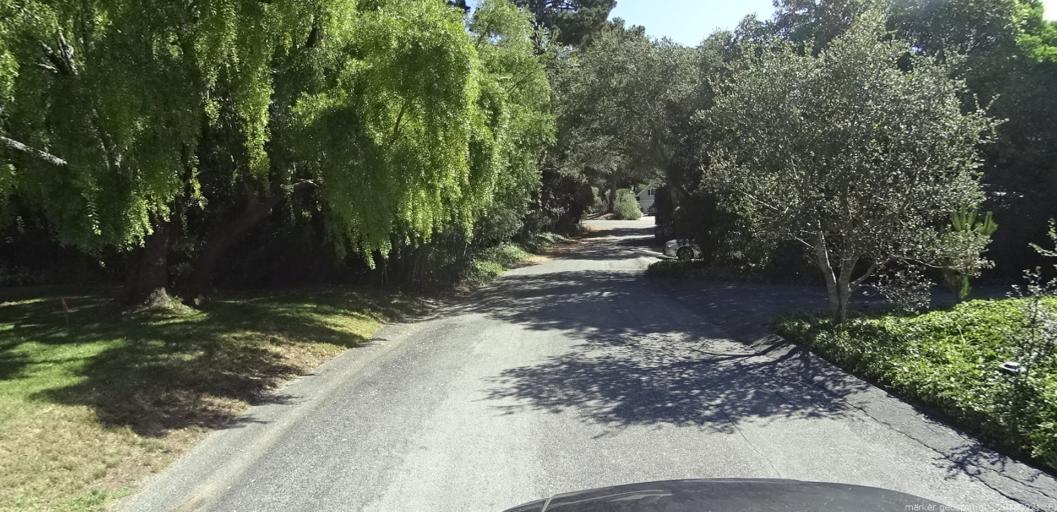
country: US
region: California
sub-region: Monterey County
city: Carmel-by-the-Sea
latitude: 36.5562
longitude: -121.9140
